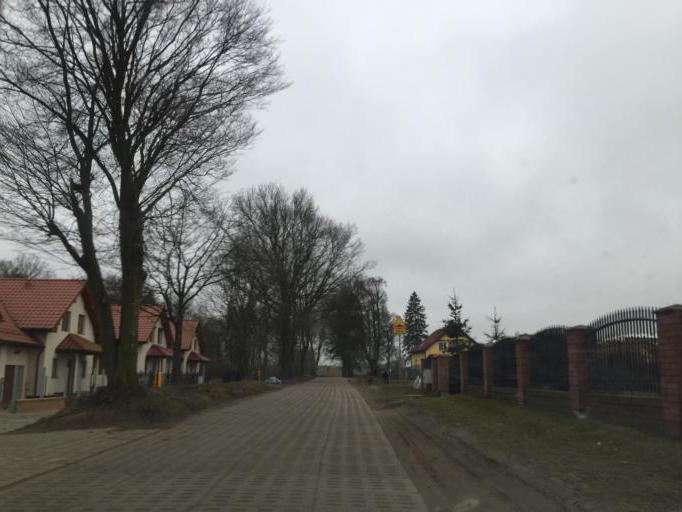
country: PL
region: Pomeranian Voivodeship
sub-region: Powiat kartuski
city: Banino
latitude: 54.3774
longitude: 18.4075
